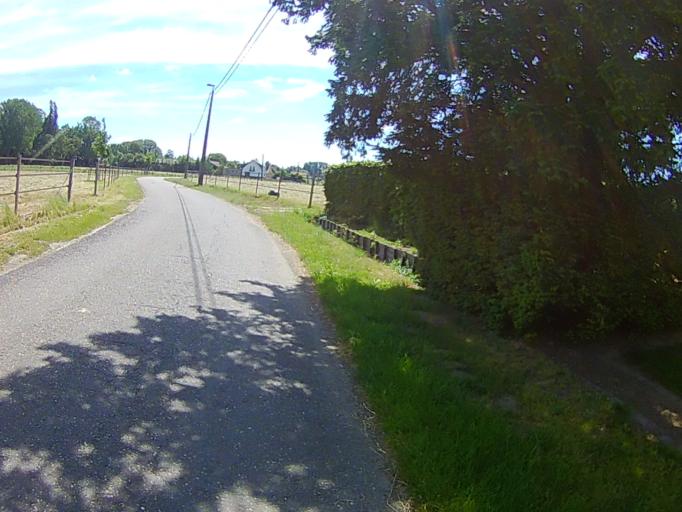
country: BE
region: Flanders
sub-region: Provincie Antwerpen
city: Zandhoven
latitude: 51.1819
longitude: 4.6260
